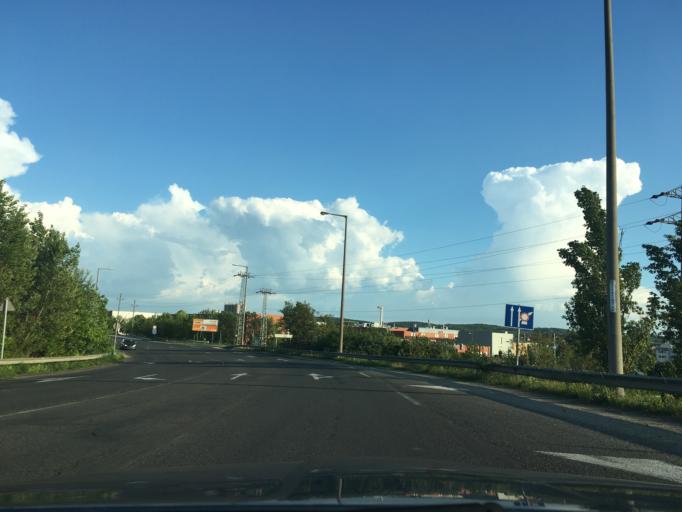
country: HU
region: Pest
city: Toeroekbalint
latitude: 47.4587
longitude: 18.9025
